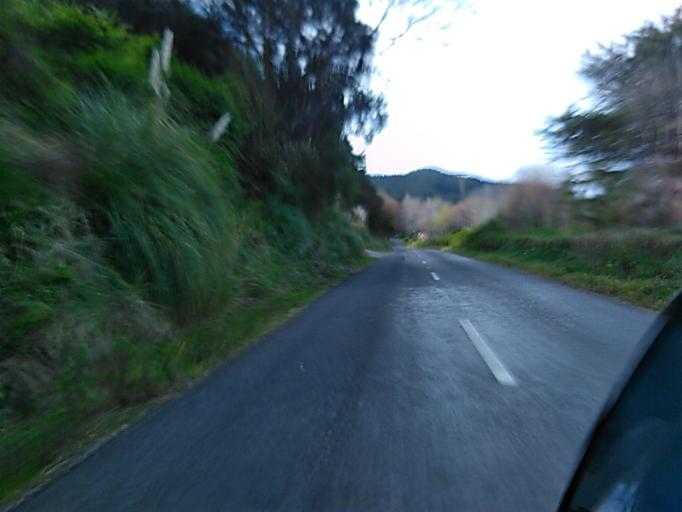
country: NZ
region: Gisborne
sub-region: Gisborne District
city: Gisborne
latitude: -38.6561
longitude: 178.0503
